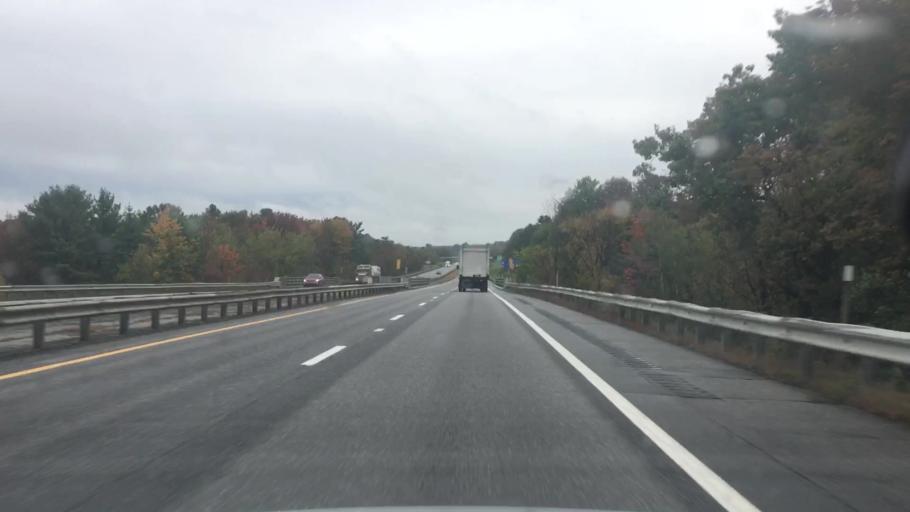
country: US
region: Maine
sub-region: Kennebec County
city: Hallowell
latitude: 44.2881
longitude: -69.8068
